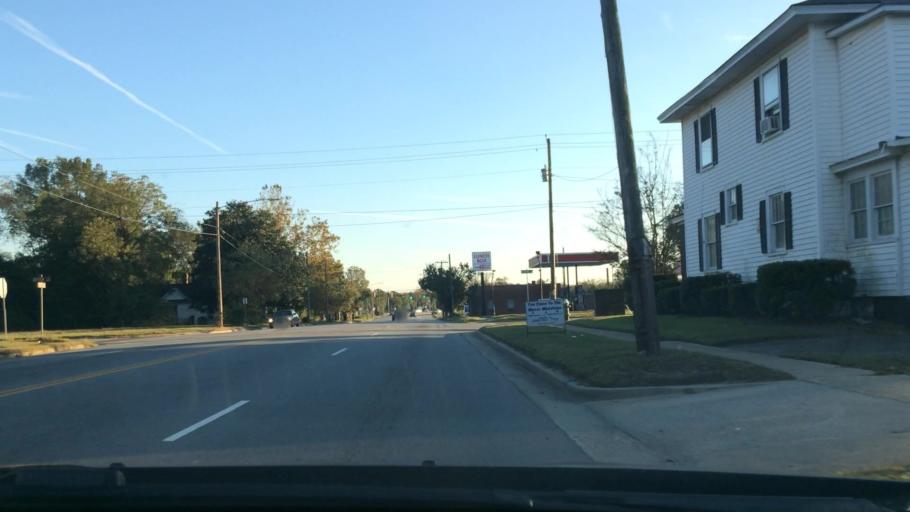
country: US
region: North Carolina
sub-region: Lenoir County
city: Kinston
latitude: 35.2619
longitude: -77.5727
